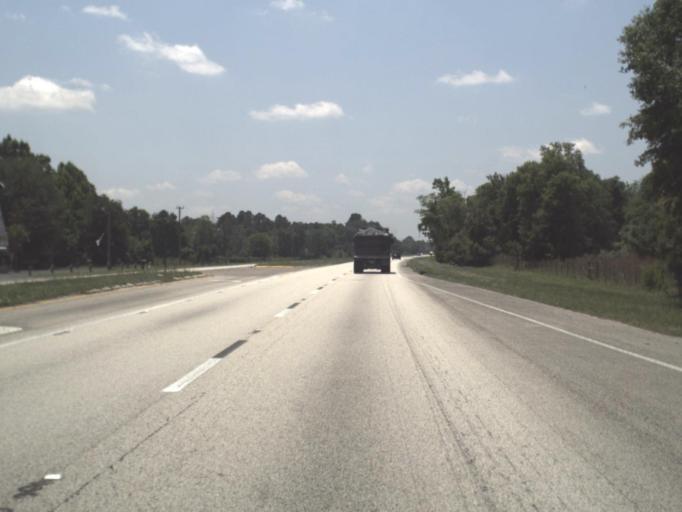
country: US
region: Florida
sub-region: Bradford County
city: Starke
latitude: 30.0339
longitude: -82.0763
